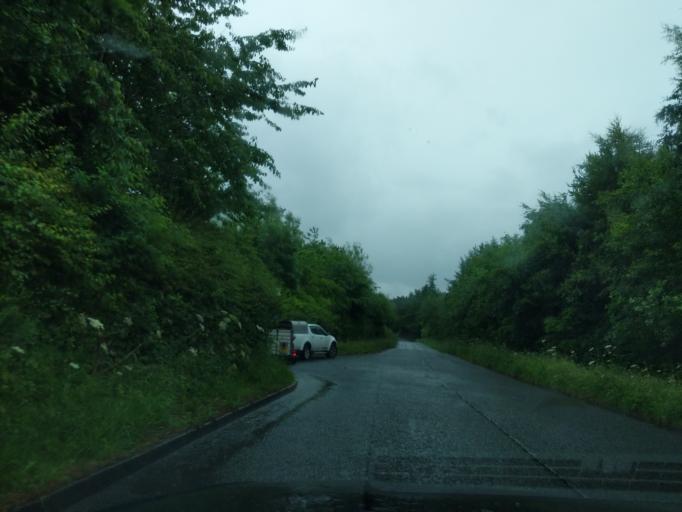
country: GB
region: Scotland
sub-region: Midlothian
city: Loanhead
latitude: 55.8503
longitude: -3.1863
